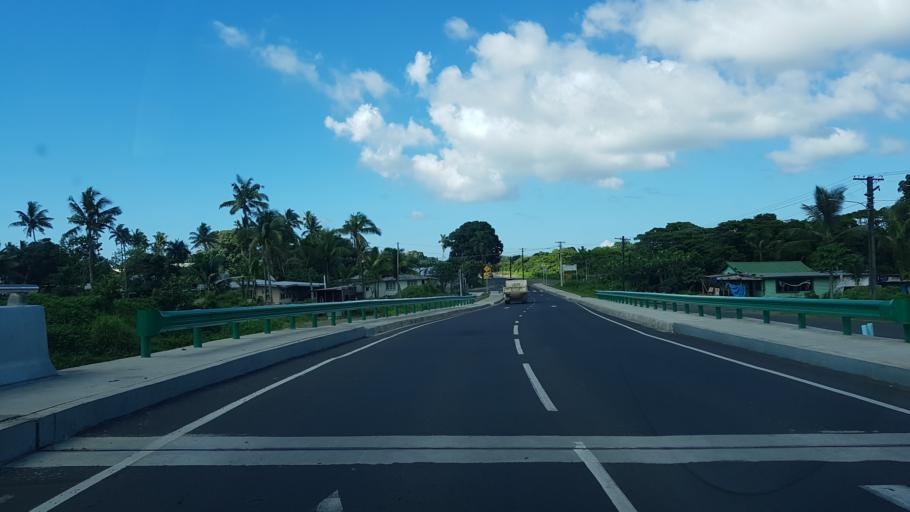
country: FJ
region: Central
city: Suva
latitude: -18.1388
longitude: 178.4582
